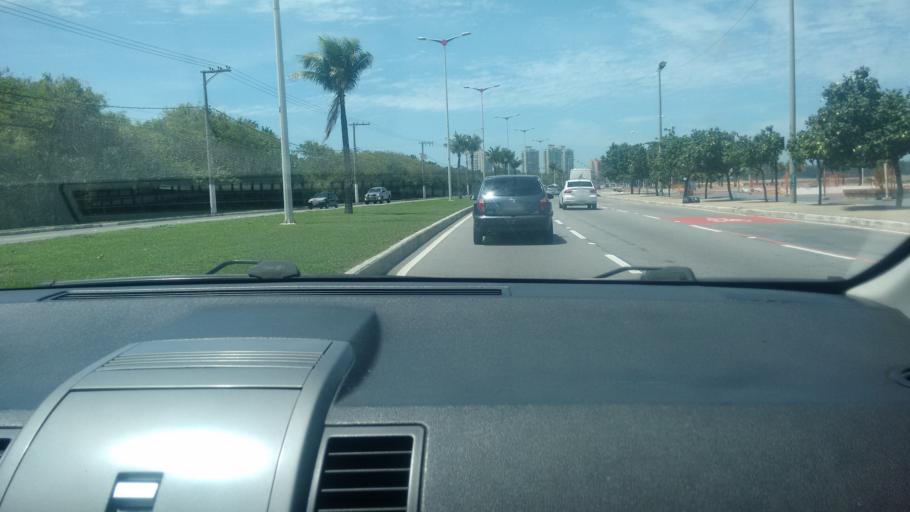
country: BR
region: Espirito Santo
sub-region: Vila Velha
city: Vila Velha
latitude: -20.2730
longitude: -40.2800
